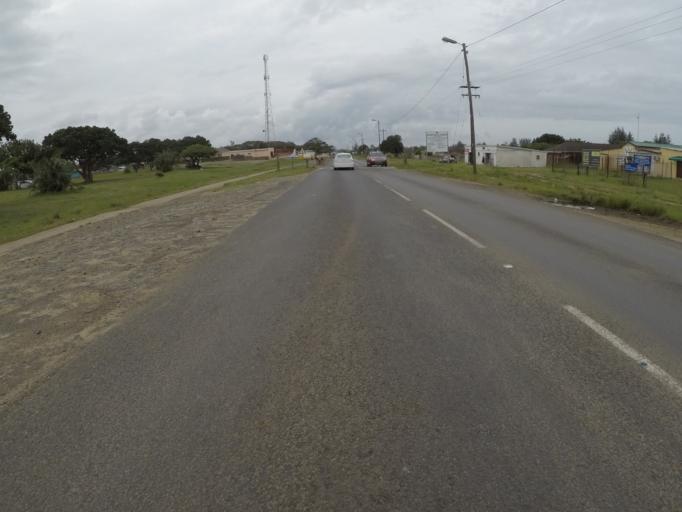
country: ZA
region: KwaZulu-Natal
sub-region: uThungulu District Municipality
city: Richards Bay
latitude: -28.7631
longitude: 32.1318
